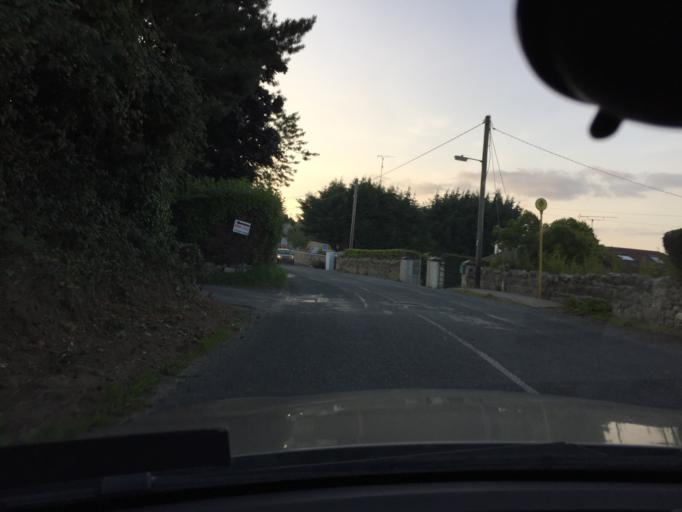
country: IE
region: Leinster
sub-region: Wicklow
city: Enniskerry
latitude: 53.1958
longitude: -6.1922
